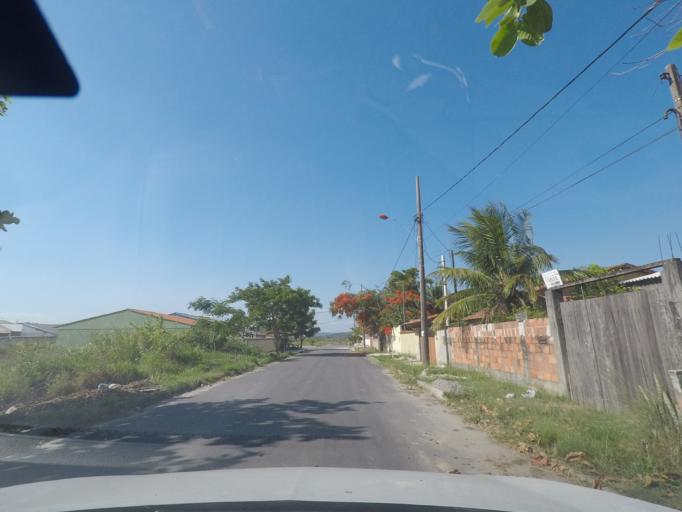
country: BR
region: Rio de Janeiro
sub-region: Marica
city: Marica
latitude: -22.9656
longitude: -42.9217
